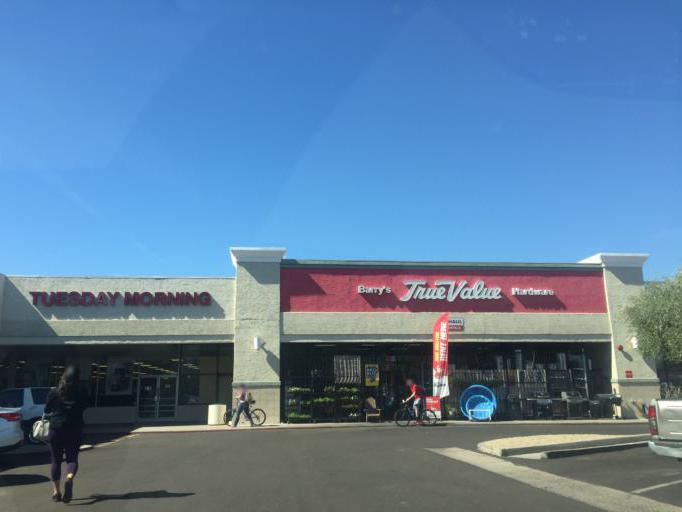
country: US
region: Arizona
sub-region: Maricopa County
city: Phoenix
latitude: 33.5513
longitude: -112.0577
